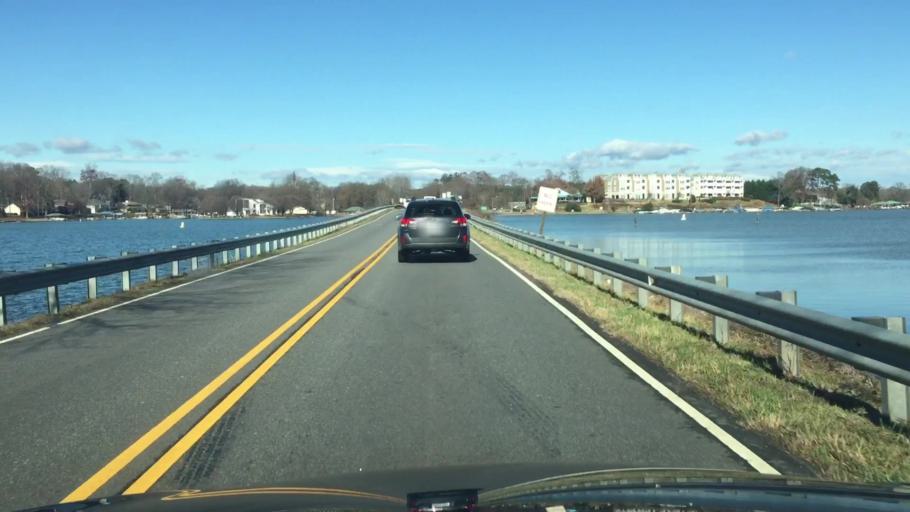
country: US
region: North Carolina
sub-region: Iredell County
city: Mooresville
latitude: 35.5628
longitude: -80.8656
